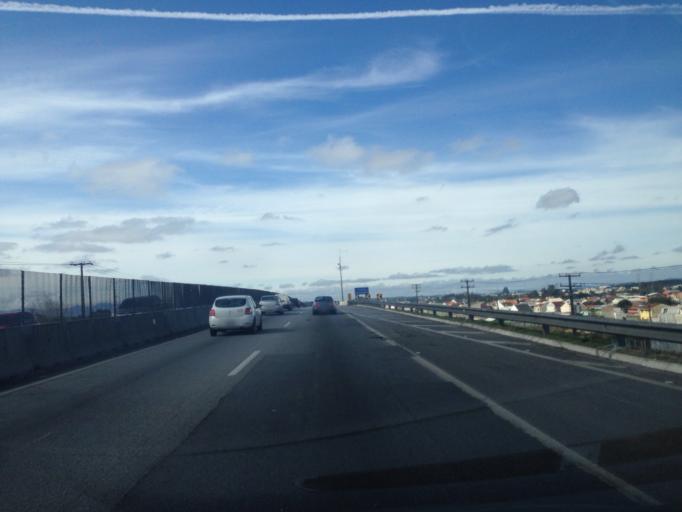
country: BR
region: Parana
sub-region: Pinhais
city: Pinhais
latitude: -25.4792
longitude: -49.2005
